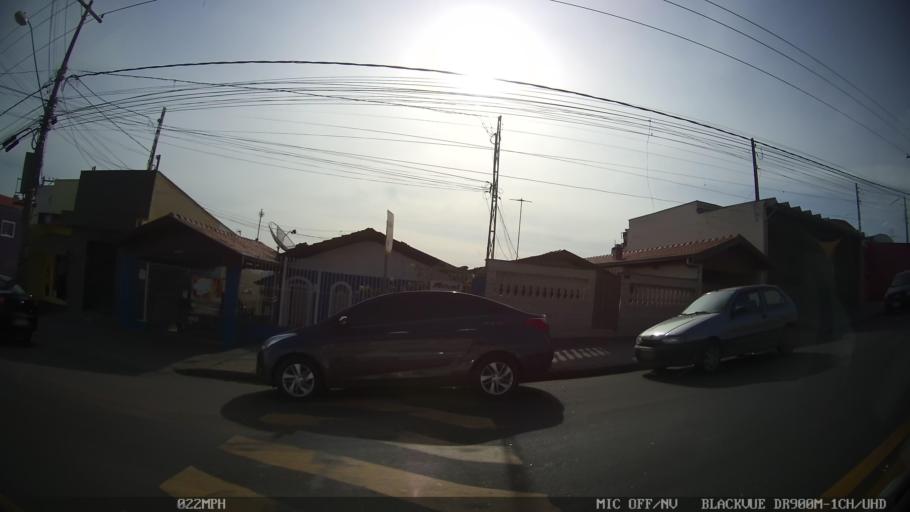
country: BR
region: Sao Paulo
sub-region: Piracicaba
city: Piracicaba
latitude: -22.7467
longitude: -47.6599
